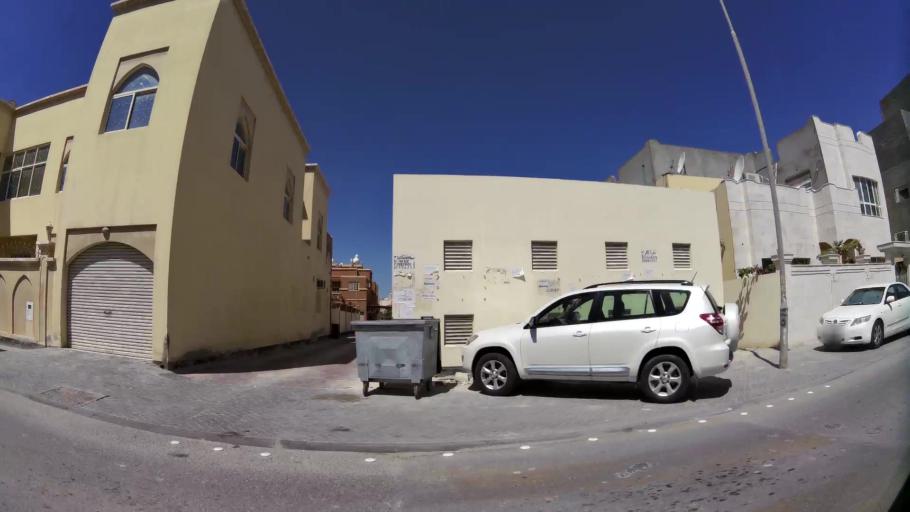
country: BH
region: Muharraq
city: Al Muharraq
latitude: 26.2763
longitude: 50.6056
